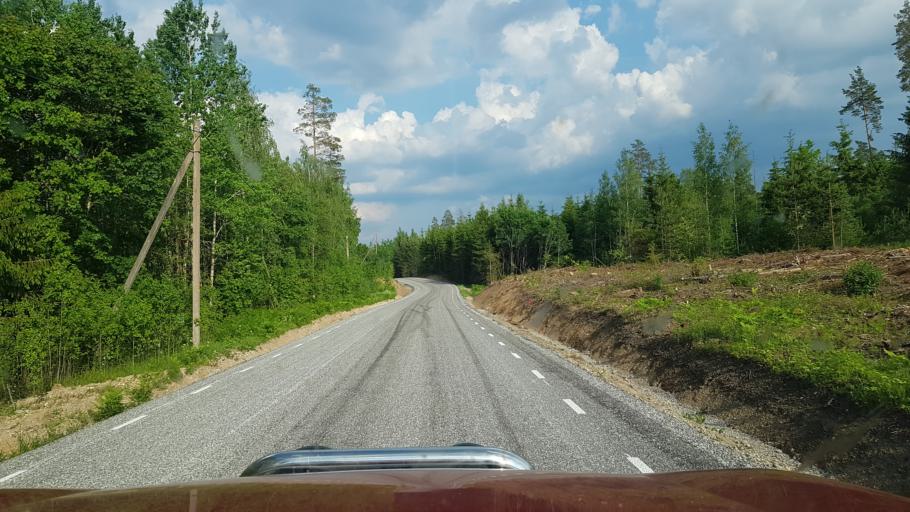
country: EE
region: Tartu
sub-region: UElenurme vald
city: Ulenurme
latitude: 58.1087
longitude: 26.7469
